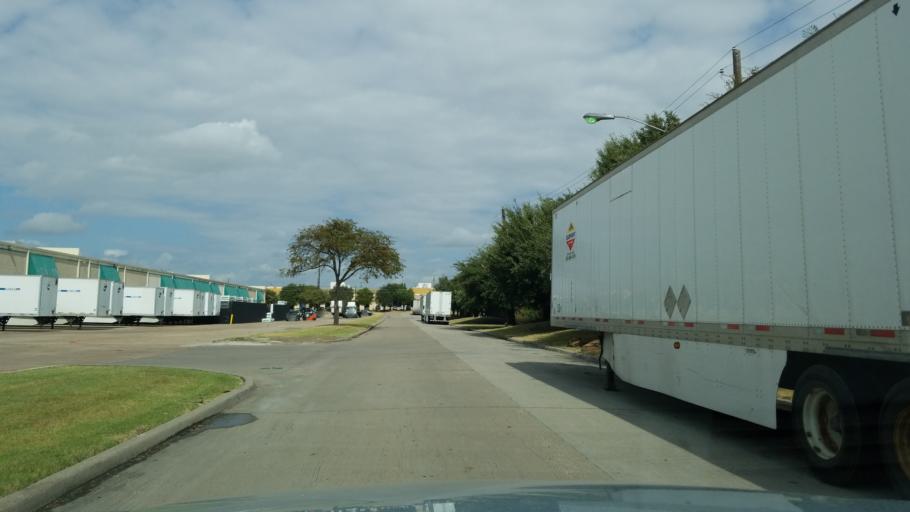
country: US
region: Texas
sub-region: Dallas County
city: Garland
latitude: 32.8922
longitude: -96.6758
